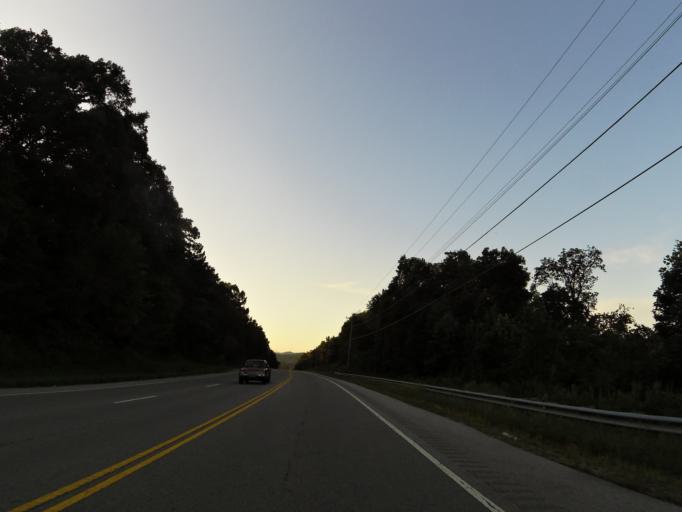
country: US
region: Tennessee
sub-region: Roane County
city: Midtown
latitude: 35.8394
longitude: -84.5422
